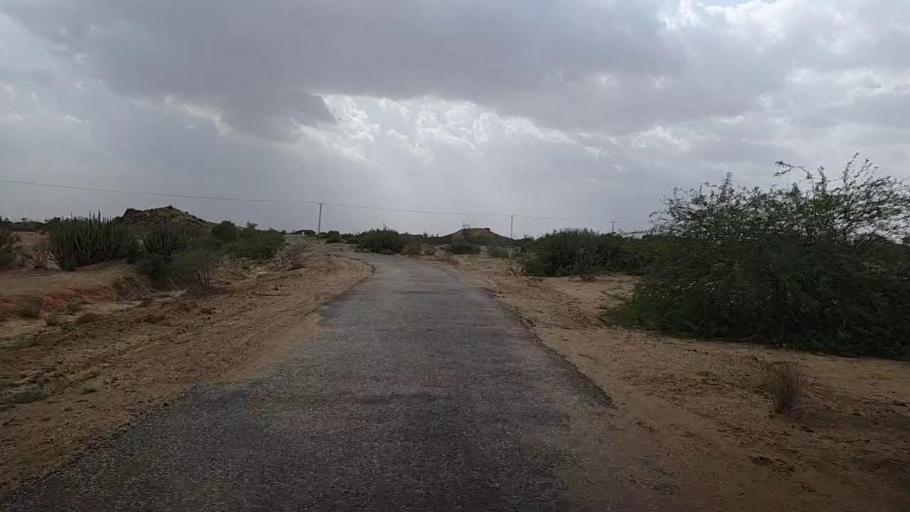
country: PK
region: Sindh
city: Jamshoro
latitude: 25.4011
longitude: 67.7131
